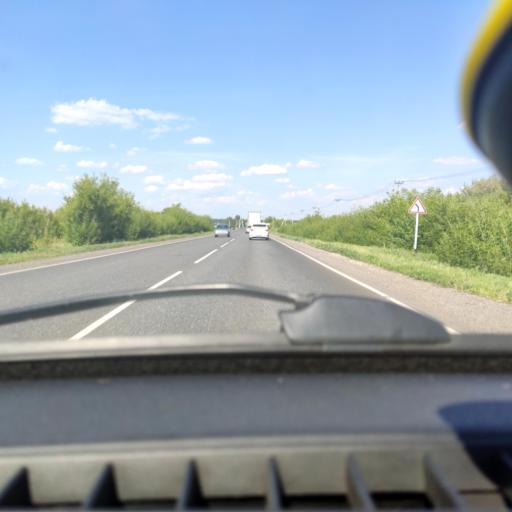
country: RU
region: Samara
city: Povolzhskiy
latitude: 53.6933
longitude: 49.7370
